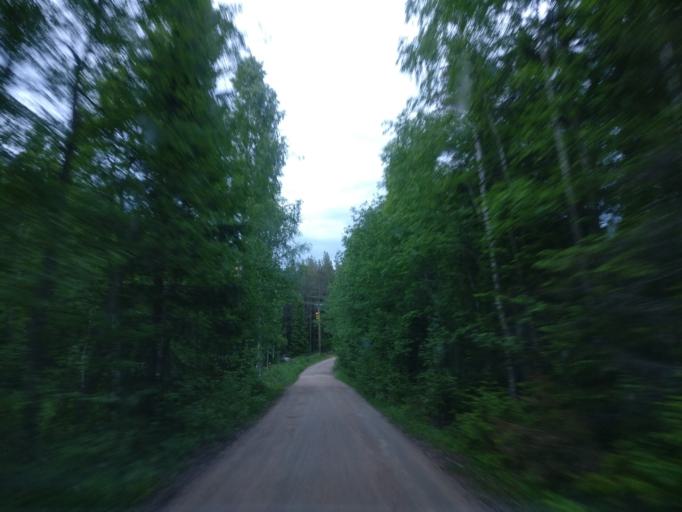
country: SE
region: Vaesternorrland
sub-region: Sundsvalls Kommun
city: Njurundabommen
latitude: 62.2087
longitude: 17.3528
